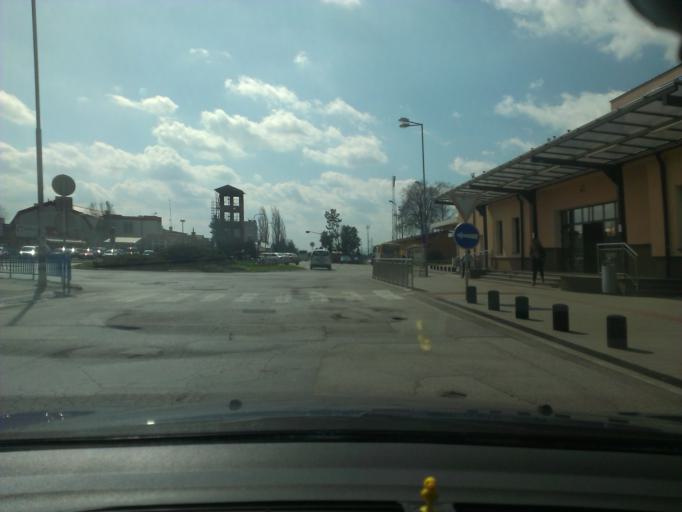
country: SK
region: Trnavsky
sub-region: Okres Trnava
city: Piestany
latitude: 48.5963
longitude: 17.8155
